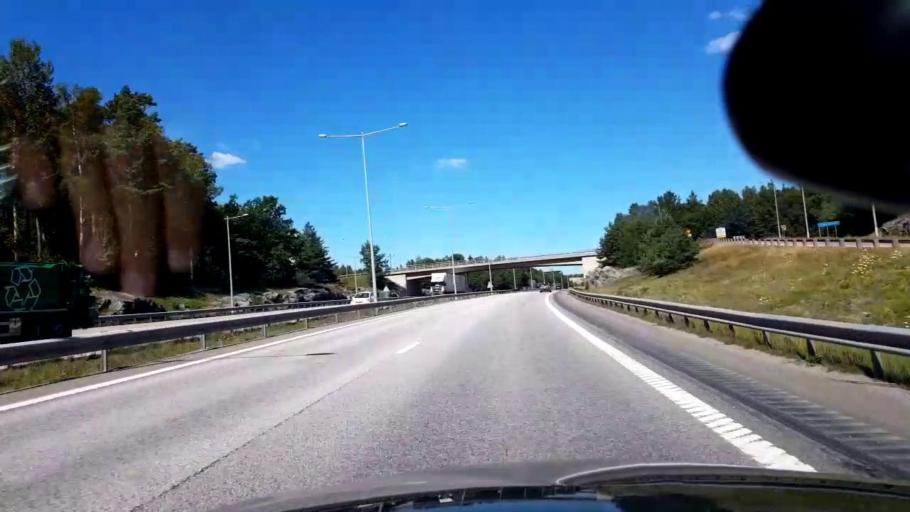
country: SE
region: Stockholm
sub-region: Upplands-Bro Kommun
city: Kungsaengen
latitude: 59.4855
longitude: 17.7599
